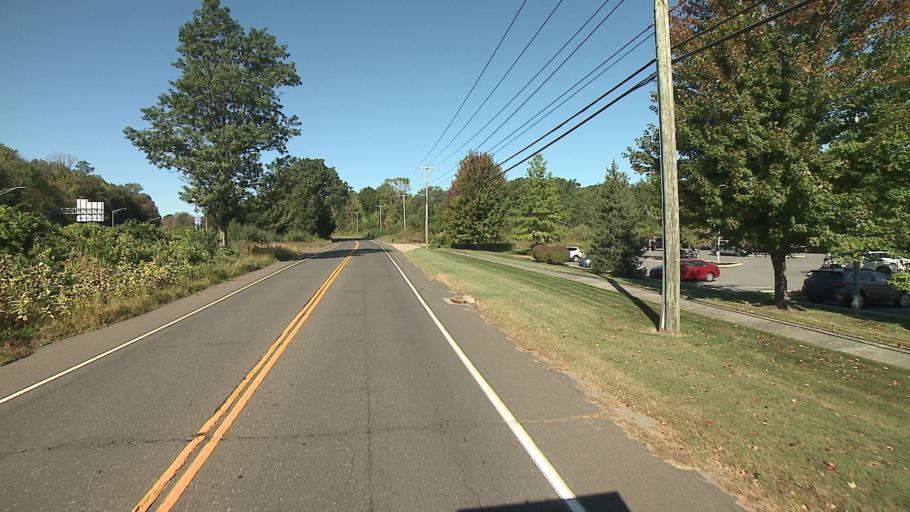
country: US
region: New York
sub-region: Putnam County
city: Peach Lake
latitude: 41.3928
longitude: -73.5262
